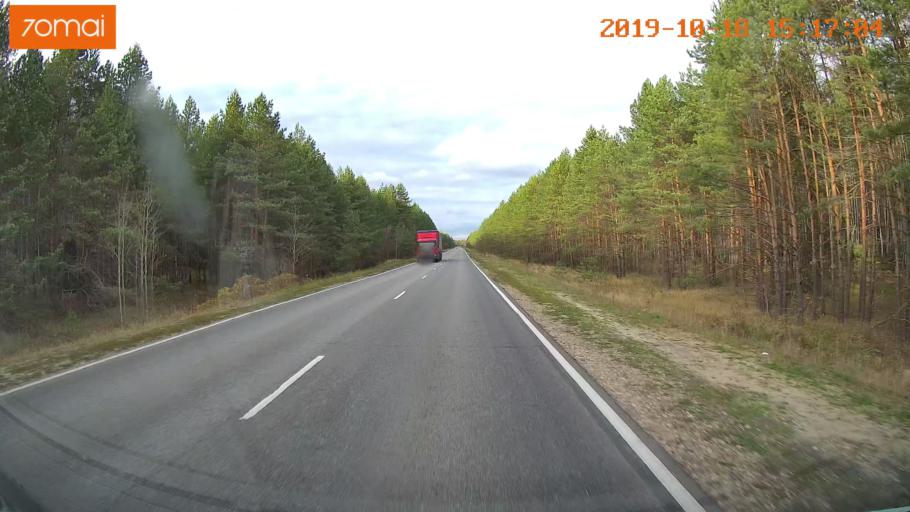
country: RU
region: Vladimir
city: Anopino
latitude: 55.6441
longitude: 40.7258
